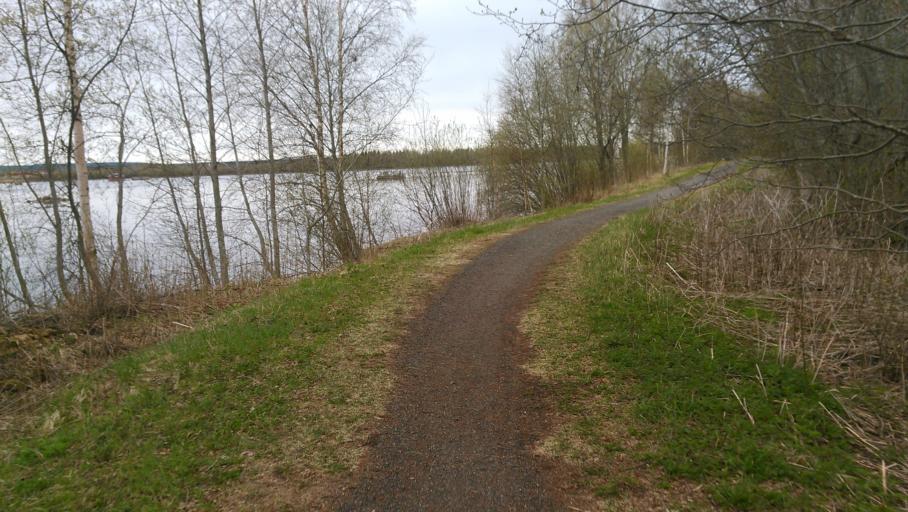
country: SE
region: Vaesterbotten
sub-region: Umea Kommun
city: Umea
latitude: 63.7802
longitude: 20.3185
